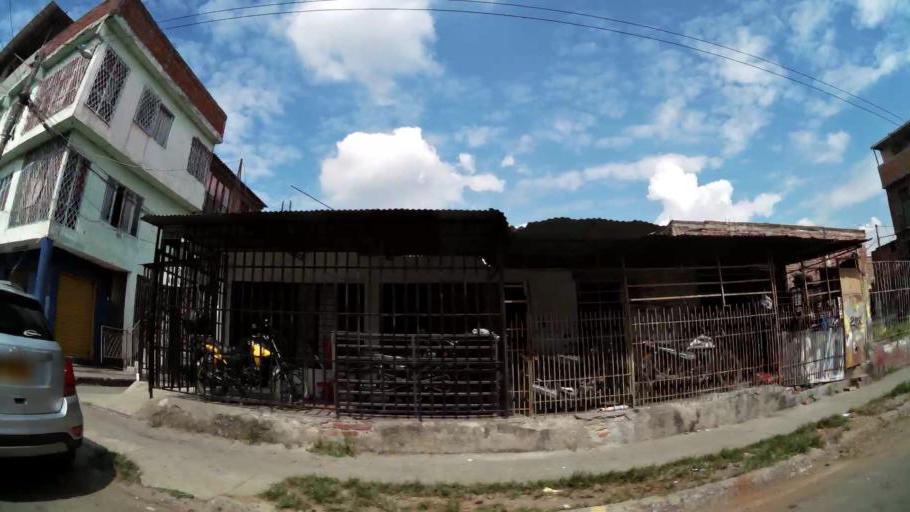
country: CO
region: Valle del Cauca
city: Cali
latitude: 3.4911
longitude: -76.4927
